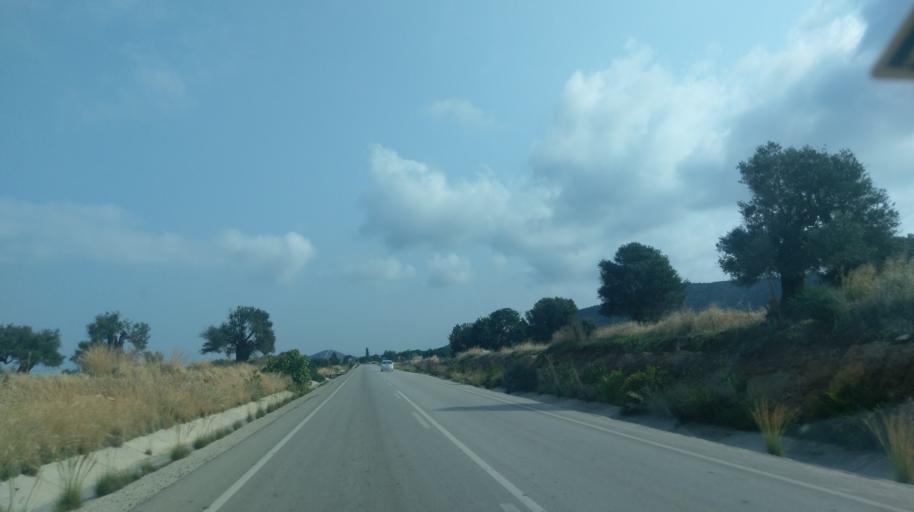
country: CY
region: Ammochostos
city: Lefkonoiko
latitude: 35.3903
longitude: 33.7340
